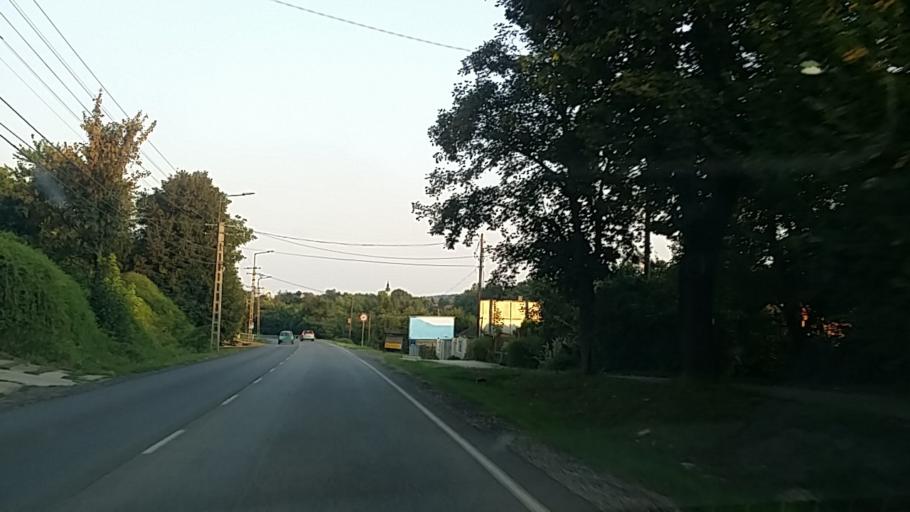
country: HU
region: Fejer
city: dunaujvaros
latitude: 46.9863
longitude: 18.9324
